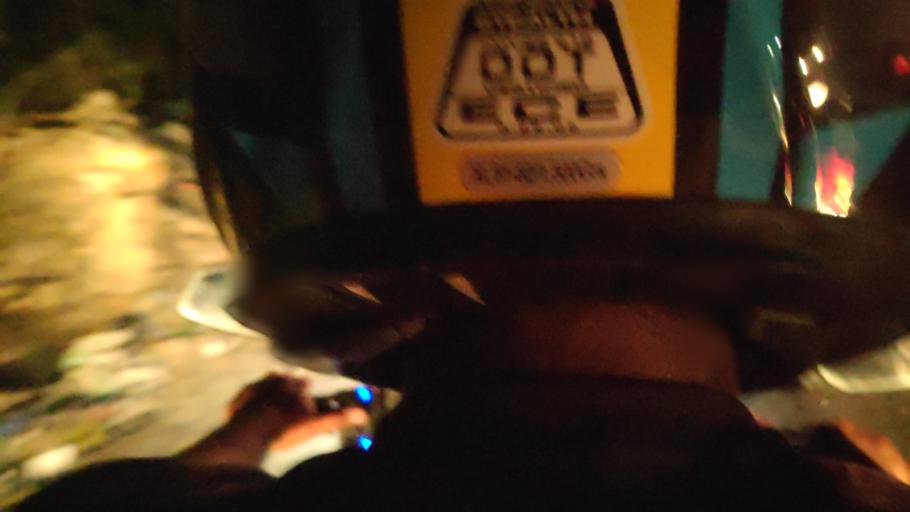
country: IN
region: Telangana
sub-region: Rangareddi
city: Kukatpalli
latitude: 17.4748
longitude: 78.3819
